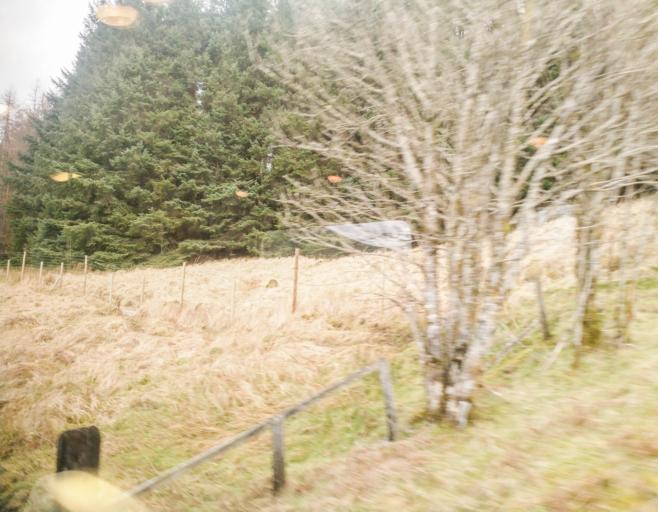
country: GB
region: Scotland
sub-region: Argyll and Bute
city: Garelochhead
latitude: 56.4395
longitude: -4.7070
